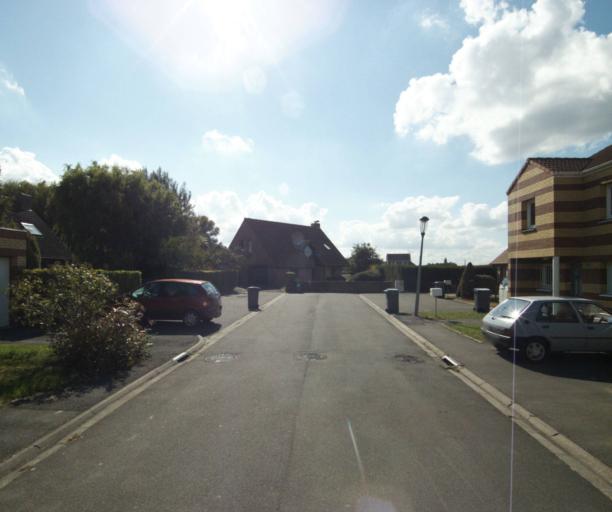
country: FR
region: Nord-Pas-de-Calais
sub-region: Departement du Nord
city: Illies
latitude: 50.5610
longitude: 2.8275
